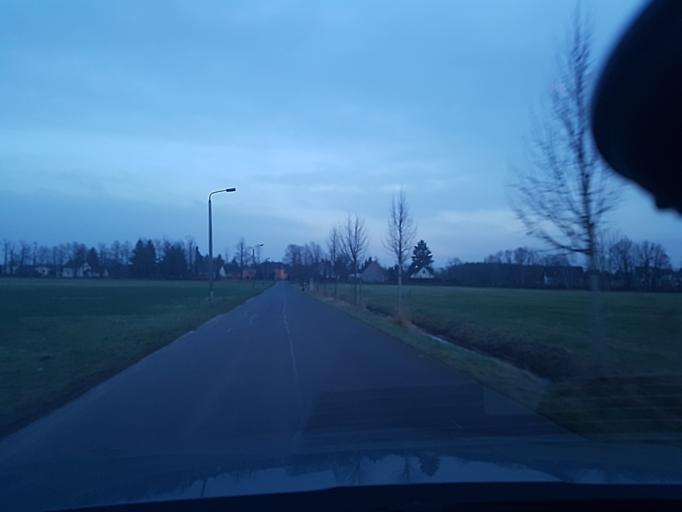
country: DE
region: Brandenburg
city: Doberlug-Kirchhain
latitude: 51.6119
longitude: 13.5559
